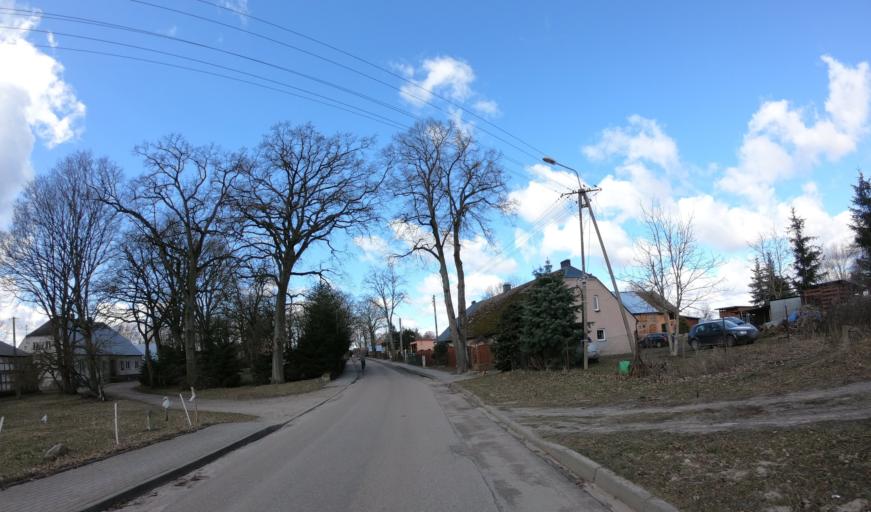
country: PL
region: West Pomeranian Voivodeship
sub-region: Powiat drawski
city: Drawsko Pomorskie
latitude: 53.4850
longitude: 15.9081
